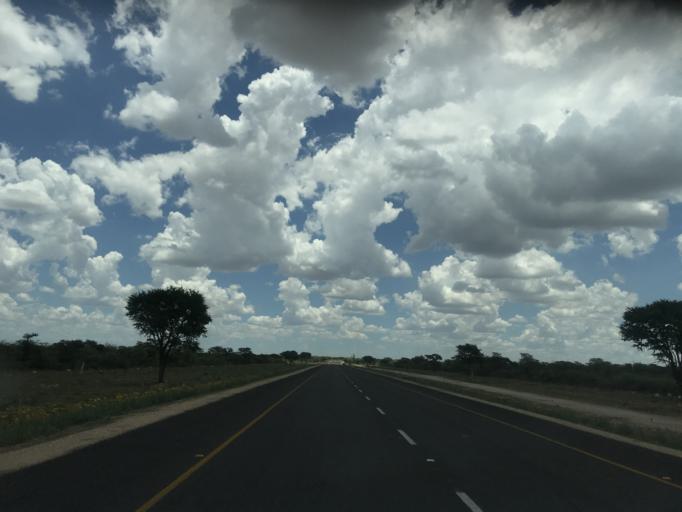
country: BW
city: Mabuli
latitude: -25.8032
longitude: 24.8344
